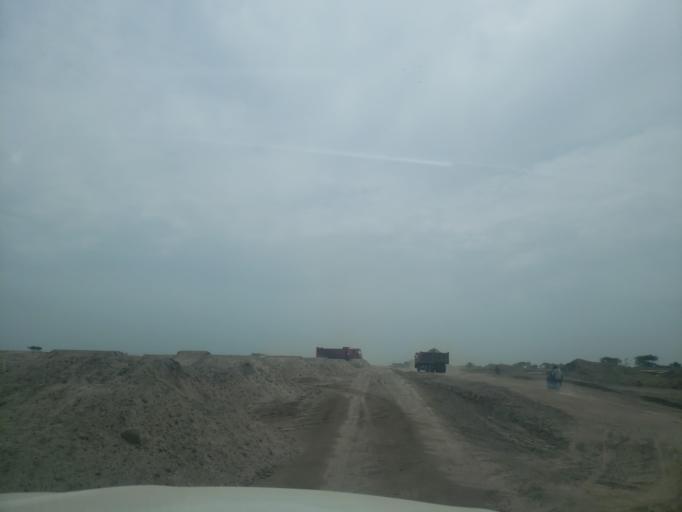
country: ET
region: Oromiya
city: Ziway
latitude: 7.8420
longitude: 38.6582
